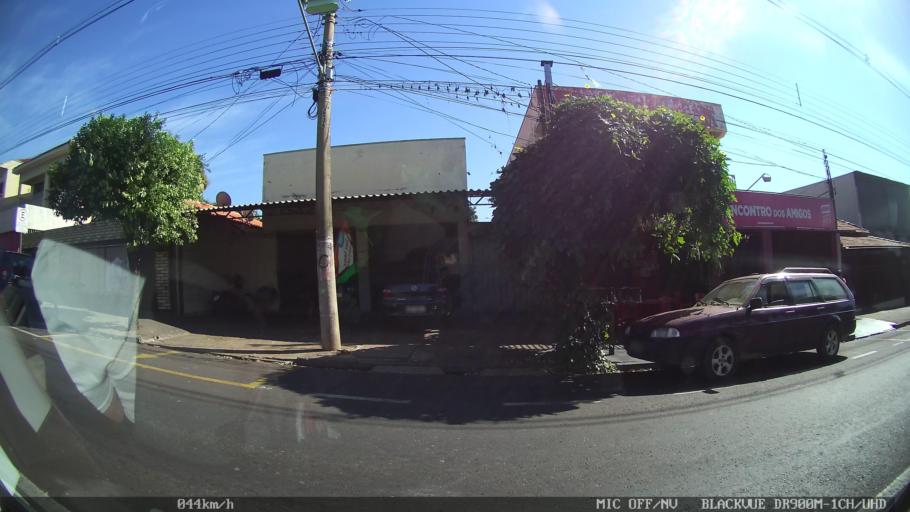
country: BR
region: Sao Paulo
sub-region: Sao Jose Do Rio Preto
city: Sao Jose do Rio Preto
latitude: -20.7721
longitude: -49.3623
